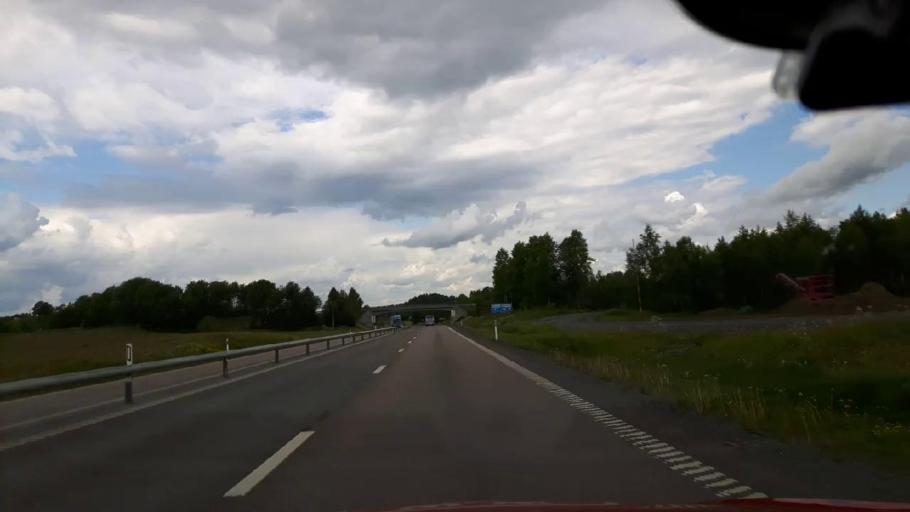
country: SE
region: Jaemtland
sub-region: Krokoms Kommun
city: Krokom
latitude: 63.3035
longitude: 14.4921
